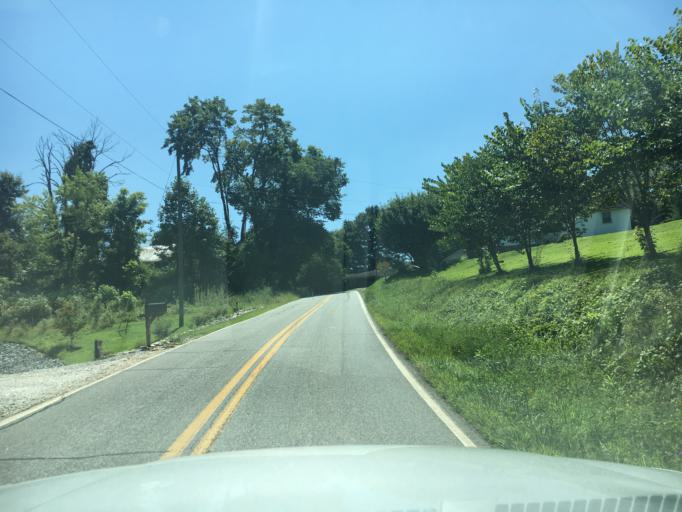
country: US
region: North Carolina
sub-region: McDowell County
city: Marion
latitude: 35.6857
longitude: -82.0327
